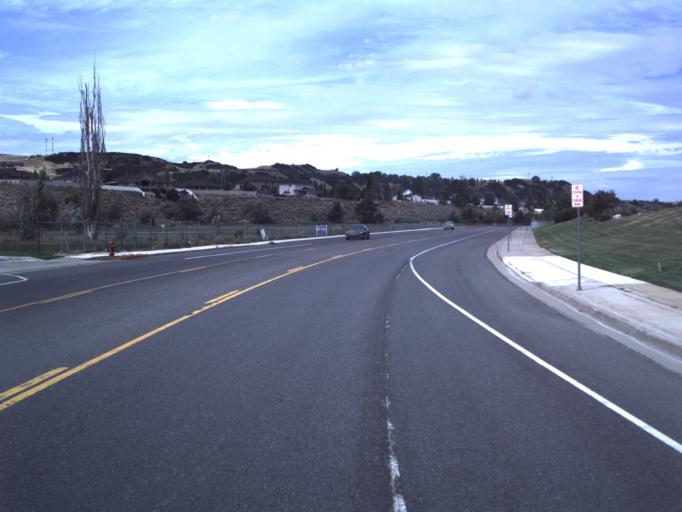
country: US
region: Utah
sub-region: Davis County
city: South Weber
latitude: 41.1269
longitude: -111.9146
